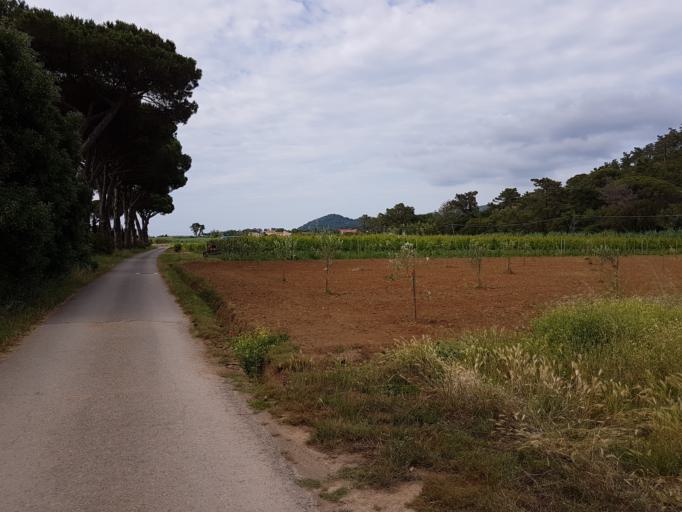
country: IT
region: Tuscany
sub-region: Provincia di Livorno
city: Portoferraio
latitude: 42.7902
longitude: 10.3497
